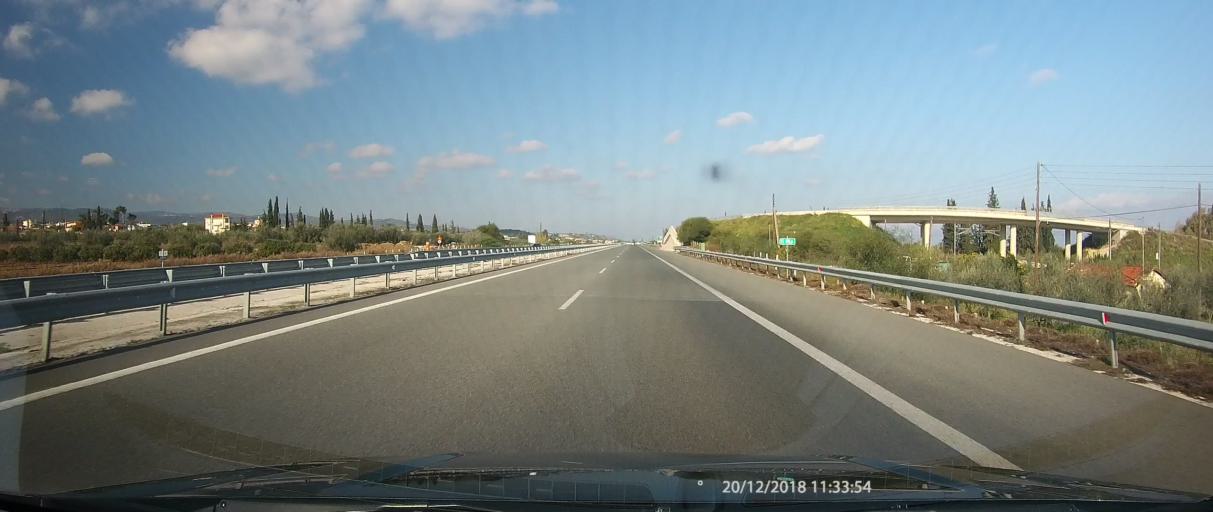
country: GR
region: Peloponnese
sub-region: Nomos Korinthias
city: Velo
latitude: 37.9513
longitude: 22.7552
